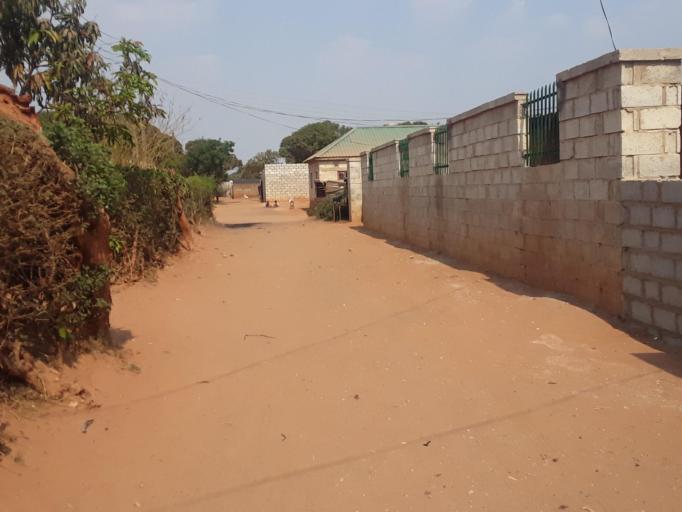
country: ZM
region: Lusaka
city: Lusaka
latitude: -15.3533
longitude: 28.2974
